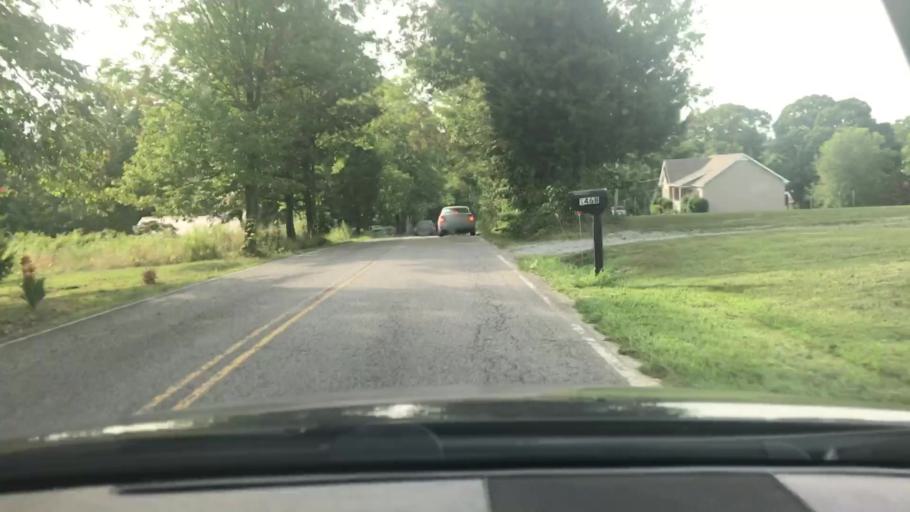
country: US
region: Tennessee
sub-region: Dickson County
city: White Bluff
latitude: 36.1595
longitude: -87.2558
